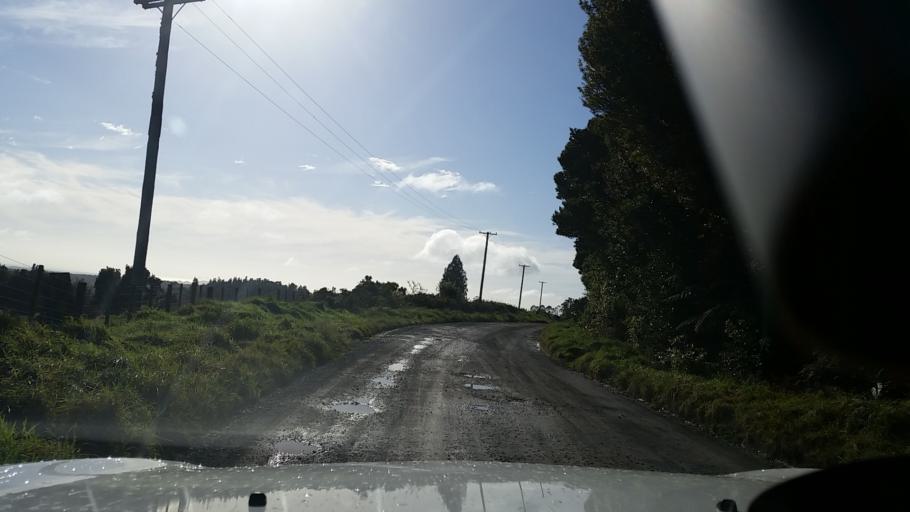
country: NZ
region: Bay of Plenty
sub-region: Rotorua District
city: Rotorua
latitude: -38.0195
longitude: 176.4640
